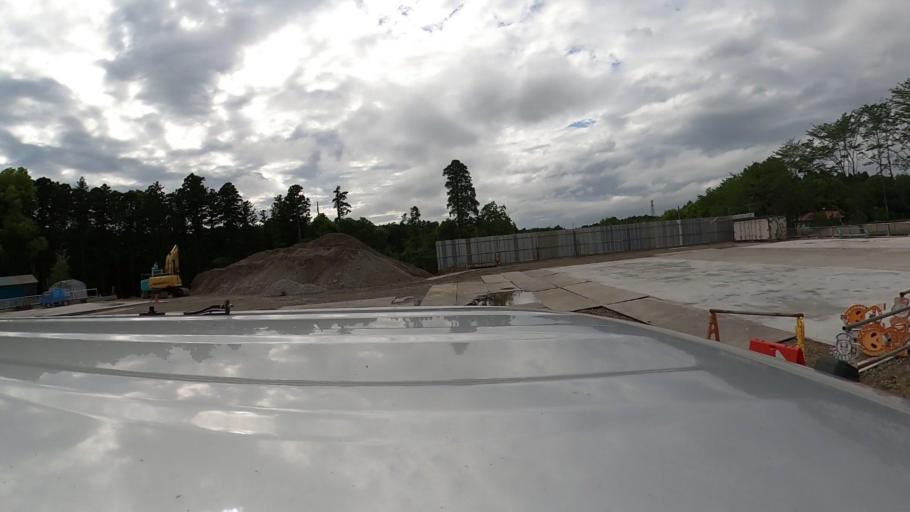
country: JP
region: Ibaraki
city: Edosaki
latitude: 35.9903
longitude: 140.2584
